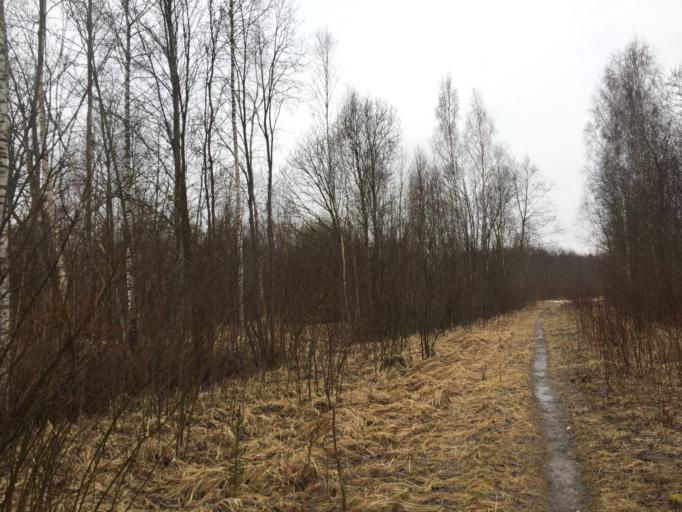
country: LV
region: Lielvarde
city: Lielvarde
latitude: 56.7277
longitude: 24.7783
